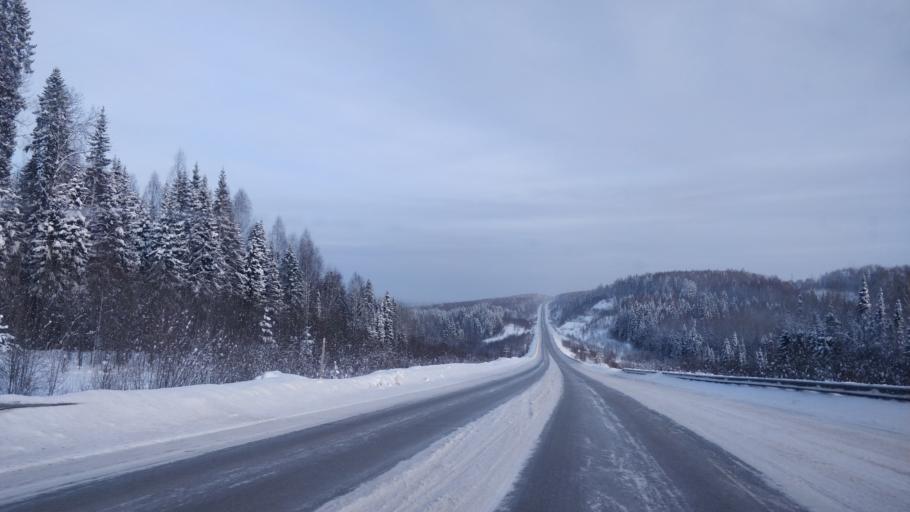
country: RU
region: Perm
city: Polazna
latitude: 58.2896
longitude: 56.5084
